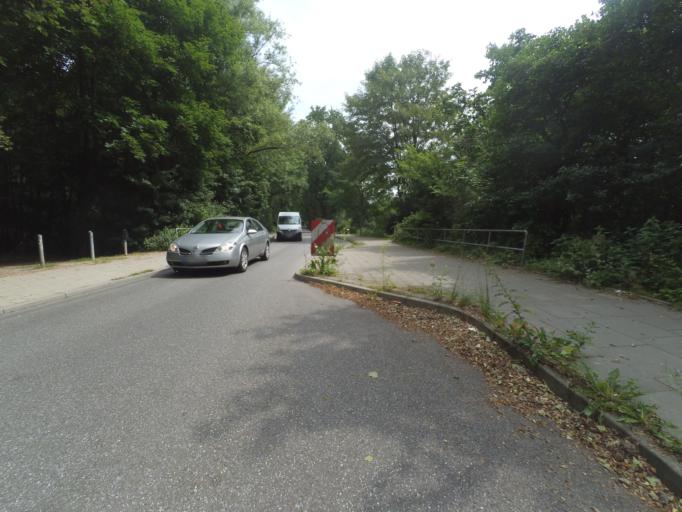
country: DE
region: Hamburg
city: Wandsbek
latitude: 53.5601
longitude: 10.1226
